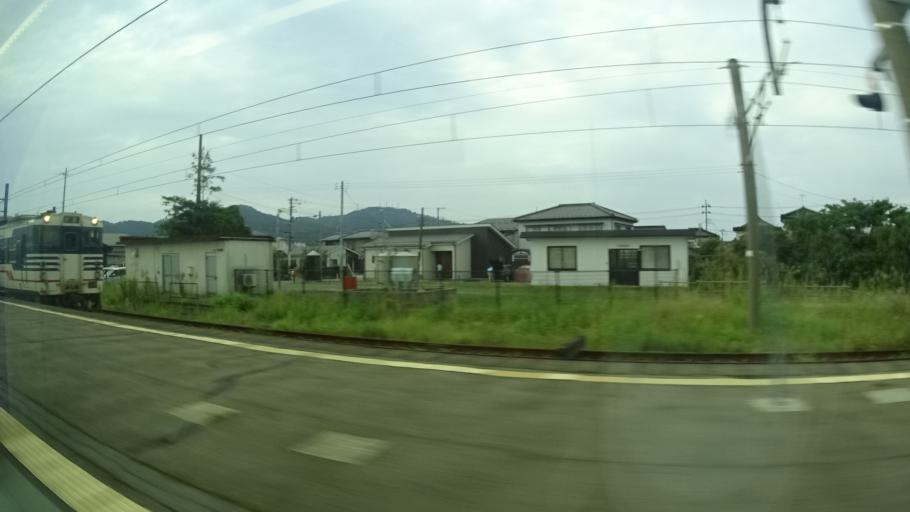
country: JP
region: Yamagata
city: Tsuruoka
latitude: 38.7421
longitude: 139.7681
